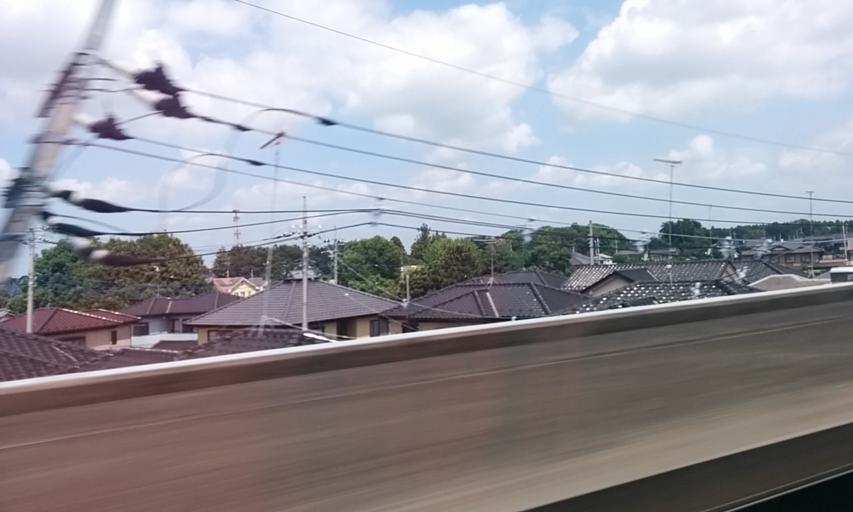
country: JP
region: Ibaraki
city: Koga
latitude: 36.1785
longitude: 139.7387
